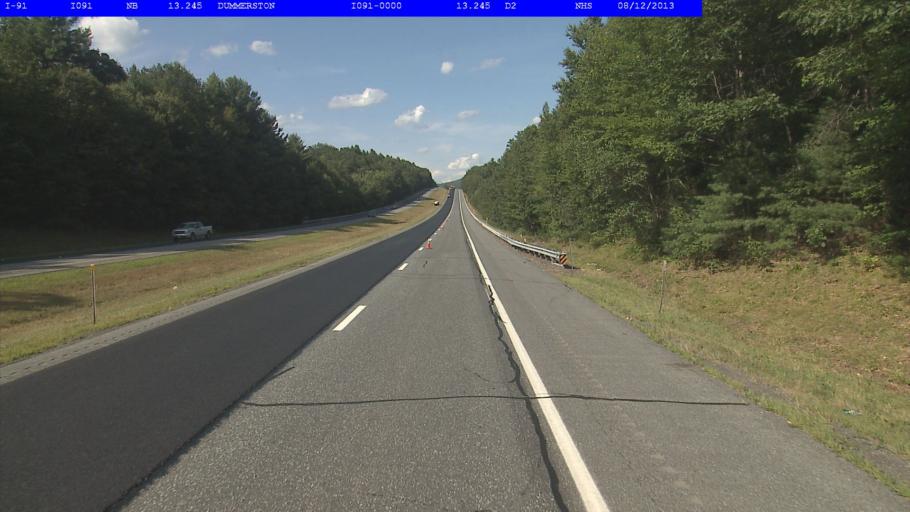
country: US
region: Vermont
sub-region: Windham County
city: Brattleboro
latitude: 42.9023
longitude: -72.5367
